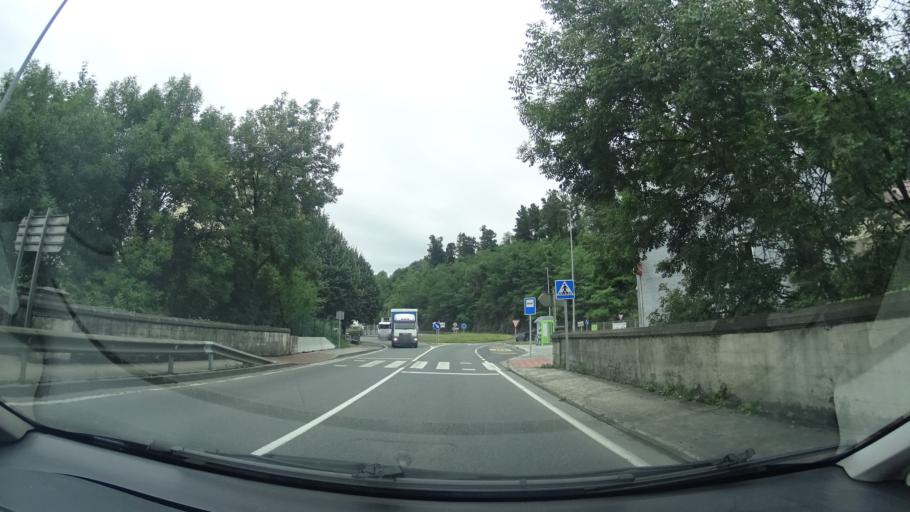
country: ES
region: Basque Country
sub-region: Bizkaia
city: Amorebieta
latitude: 43.2073
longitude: -2.7785
